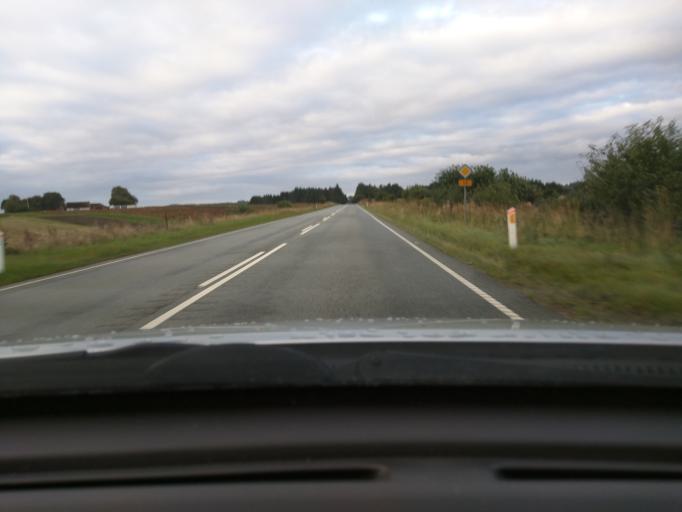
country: DK
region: Central Jutland
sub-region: Viborg Kommune
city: Viborg
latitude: 56.3703
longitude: 9.3740
